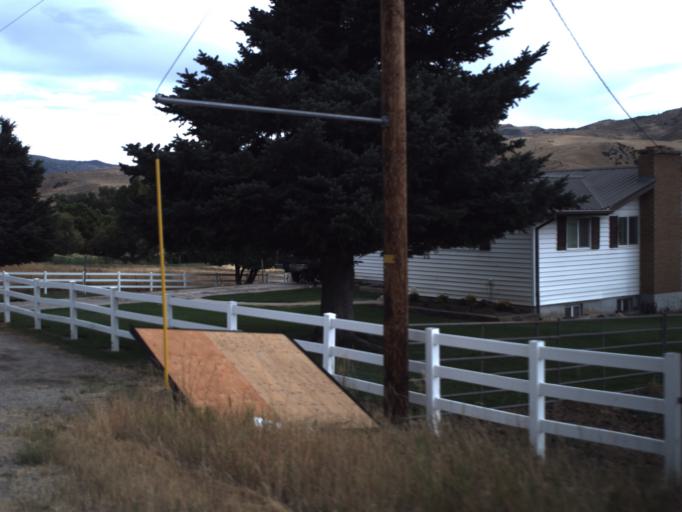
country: US
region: Utah
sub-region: Morgan County
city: Morgan
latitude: 40.9667
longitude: -111.6723
